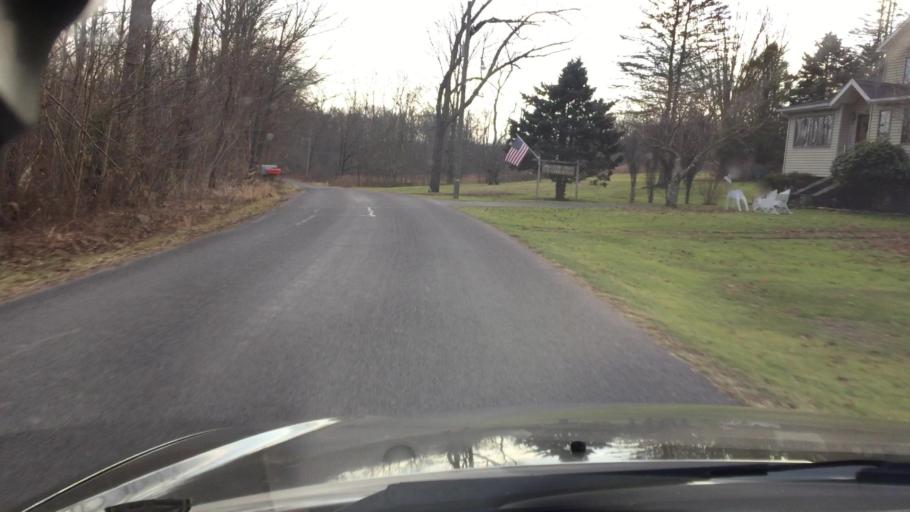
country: US
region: Pennsylvania
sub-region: Luzerne County
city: Back Mountain
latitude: 41.2930
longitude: -76.0480
